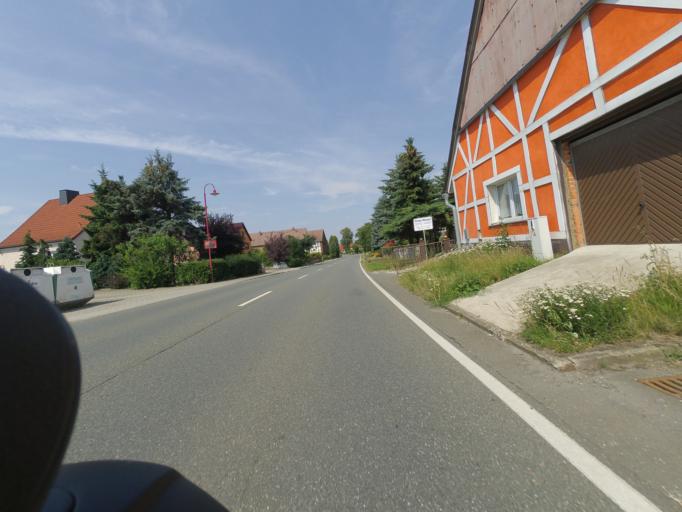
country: DE
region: Thuringia
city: Hirschfeld
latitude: 50.9661
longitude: 12.1334
